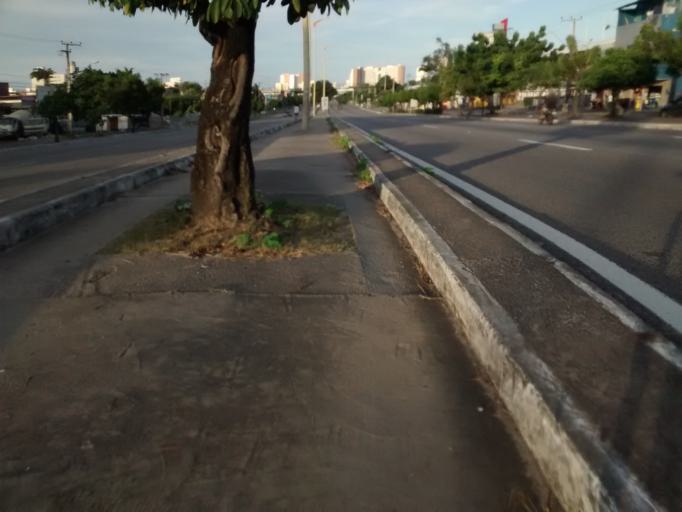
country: BR
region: Ceara
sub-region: Fortaleza
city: Fortaleza
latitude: -3.7383
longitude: -38.5817
